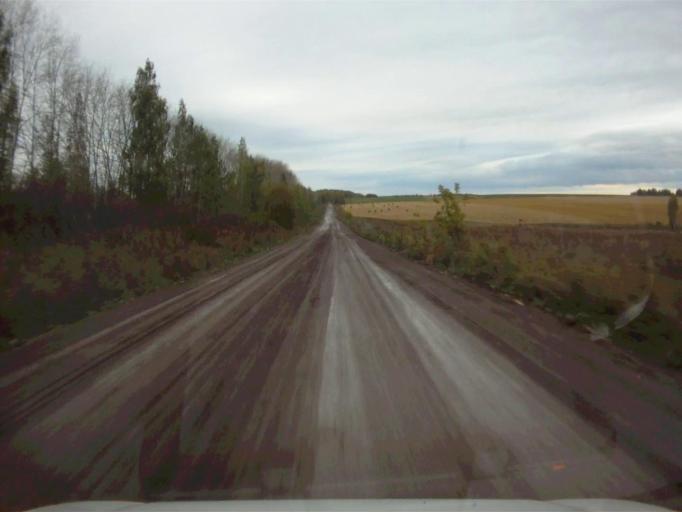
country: RU
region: Sverdlovsk
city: Mikhaylovsk
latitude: 56.1624
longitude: 59.2437
